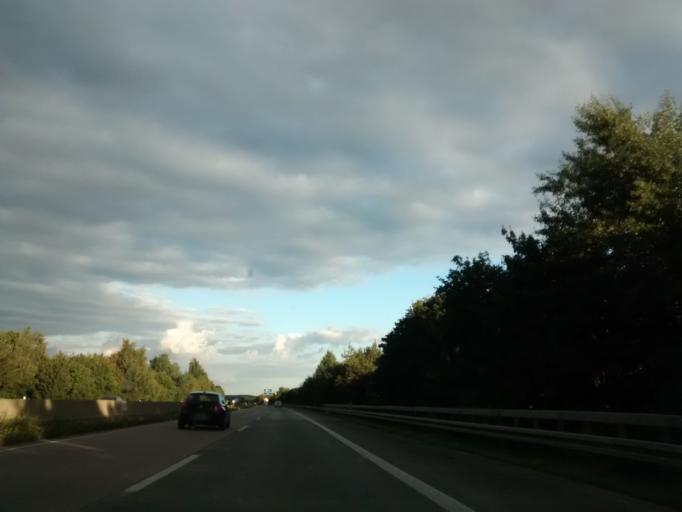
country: DE
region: North Rhine-Westphalia
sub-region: Regierungsbezirk Munster
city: Dreierwalde
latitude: 52.2938
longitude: 7.5192
